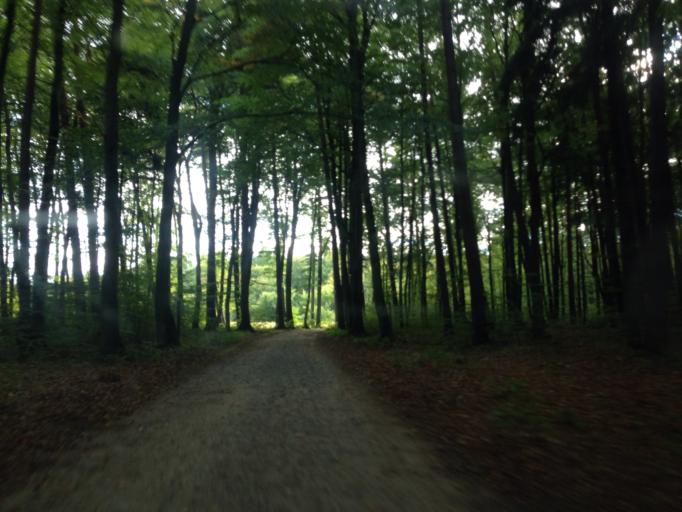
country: PL
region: Warmian-Masurian Voivodeship
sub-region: Powiat ilawski
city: Susz
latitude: 53.7663
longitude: 19.3189
